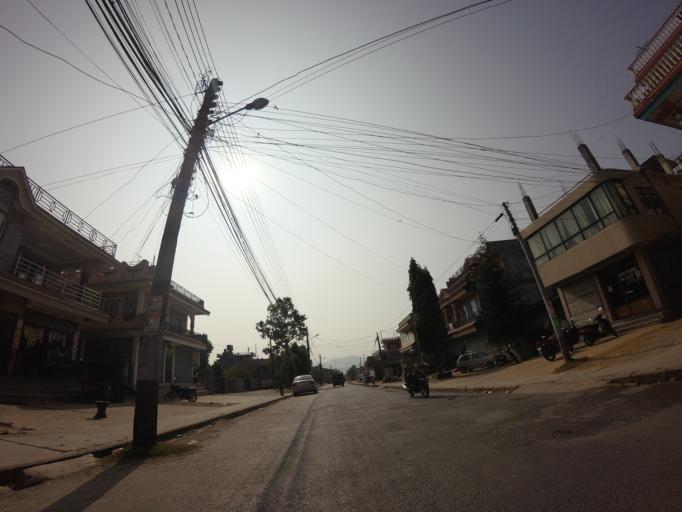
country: NP
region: Western Region
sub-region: Gandaki Zone
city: Pokhara
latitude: 28.2190
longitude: 83.9840
